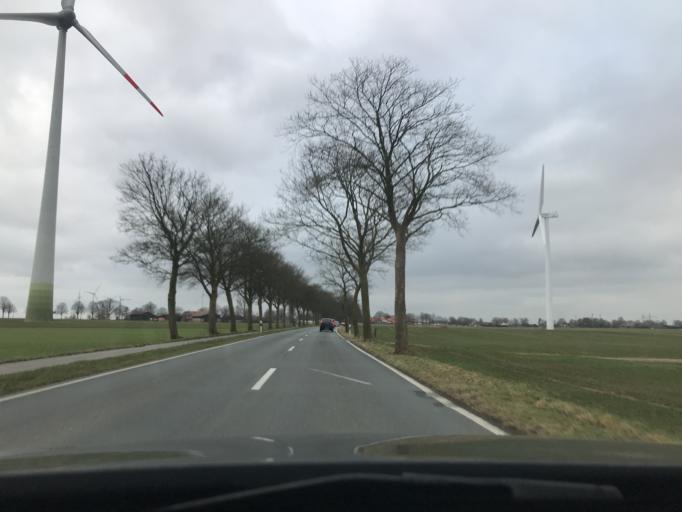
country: DE
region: North Rhine-Westphalia
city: Kalkar
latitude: 51.7106
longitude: 6.2301
